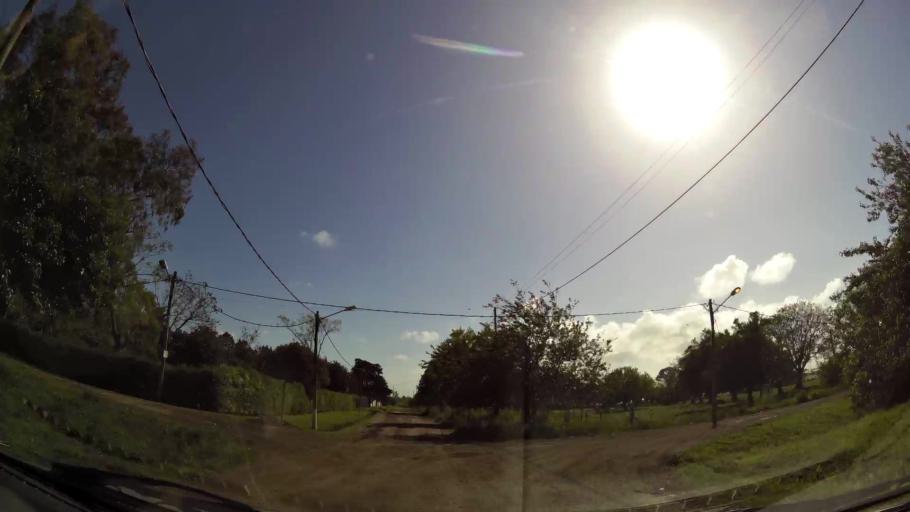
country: AR
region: Buenos Aires
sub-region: Partido de Quilmes
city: Quilmes
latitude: -34.7975
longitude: -58.1378
